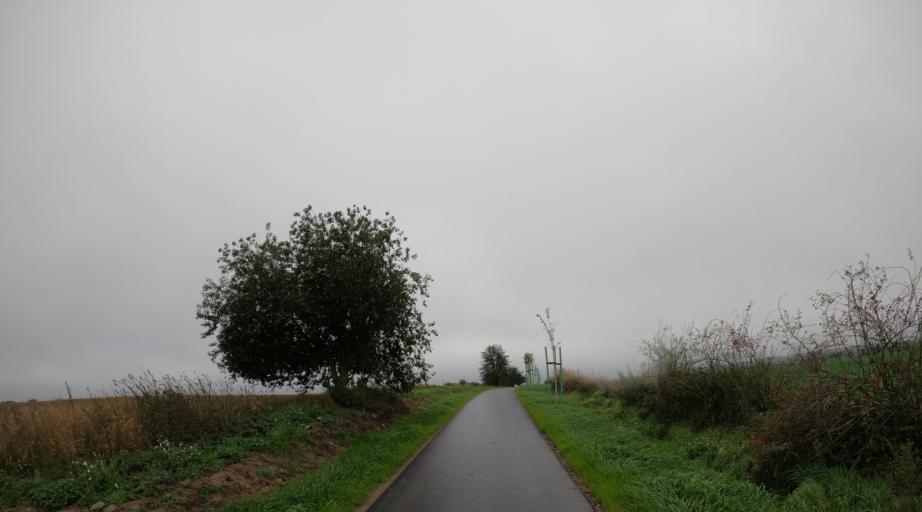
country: PL
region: West Pomeranian Voivodeship
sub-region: Powiat mysliborski
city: Mysliborz
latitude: 52.9246
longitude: 14.7345
